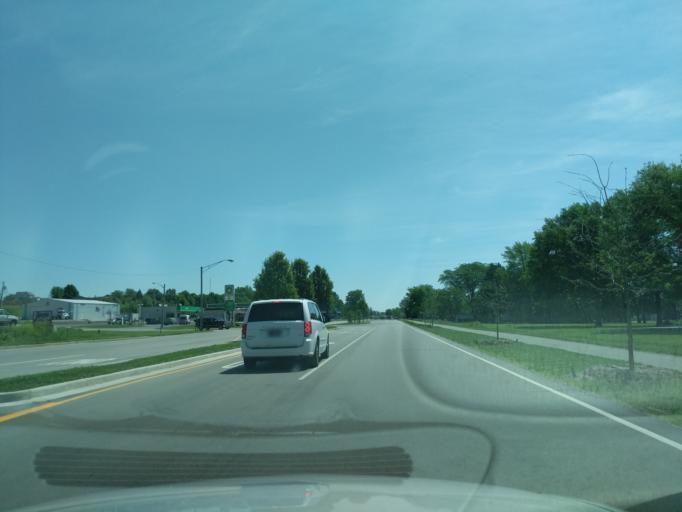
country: US
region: Indiana
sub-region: Huntington County
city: Huntington
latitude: 40.8925
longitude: -85.4856
